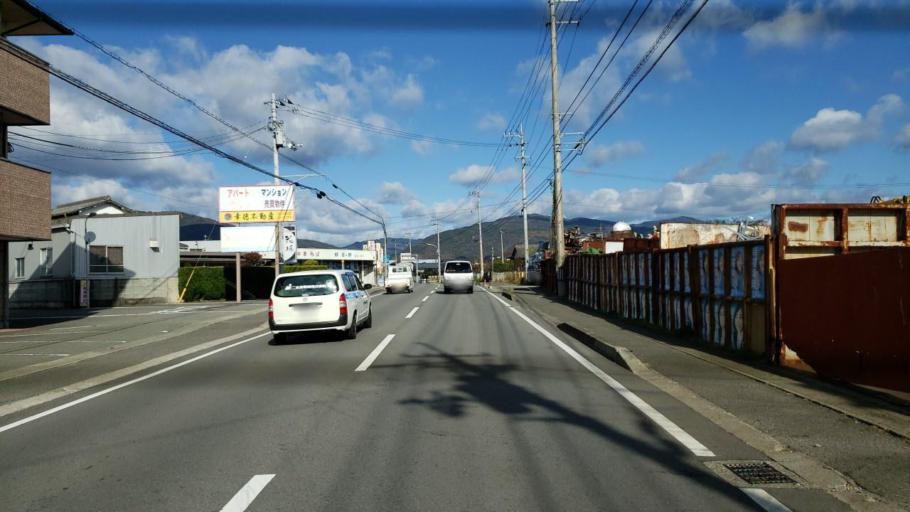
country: JP
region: Tokushima
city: Kamojimacho-jogejima
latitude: 34.0979
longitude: 134.3447
